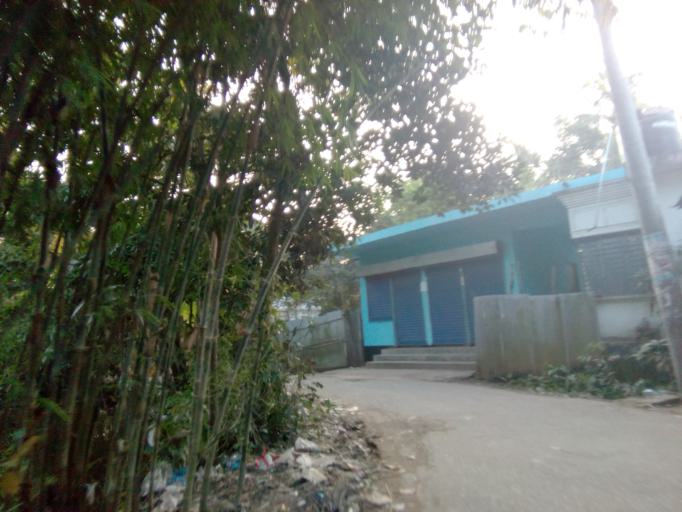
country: BD
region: Chittagong
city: Comilla
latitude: 23.4037
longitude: 91.1921
